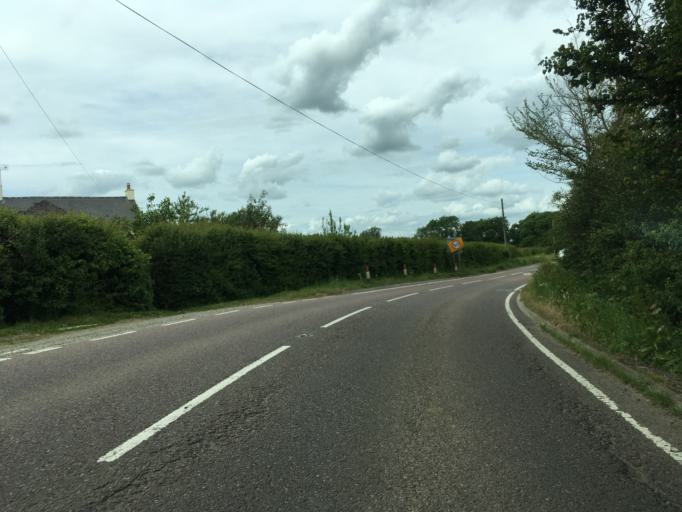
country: GB
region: England
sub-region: Wiltshire
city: Lyneham
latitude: 51.5605
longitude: -1.9908
